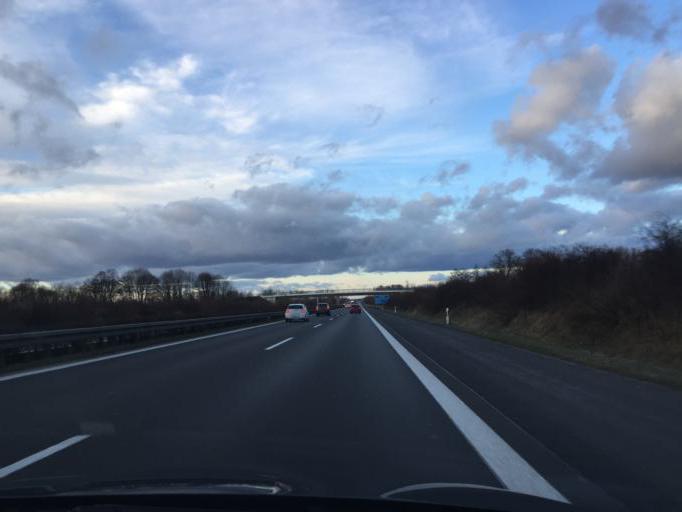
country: DE
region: Brandenburg
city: Mittenwalde
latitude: 52.2713
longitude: 13.5732
